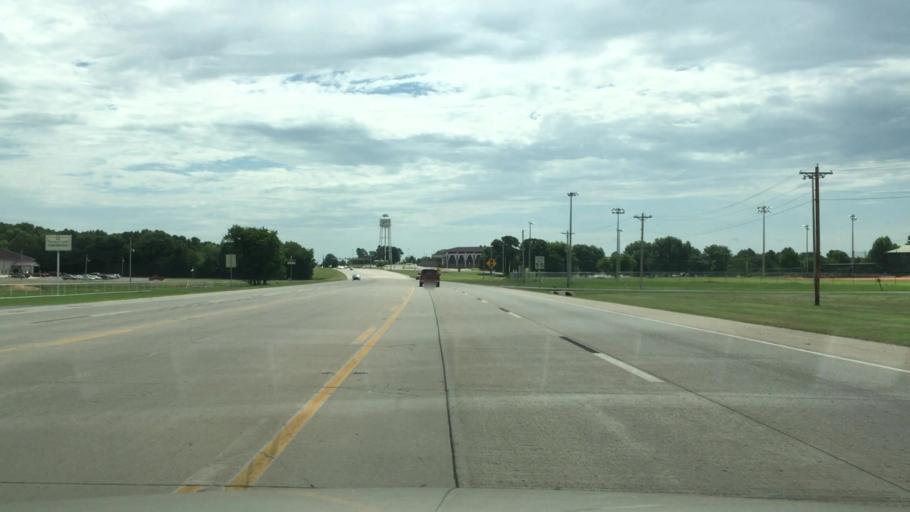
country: US
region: Oklahoma
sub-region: Cherokee County
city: Park Hill
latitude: 35.8492
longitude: -95.0097
